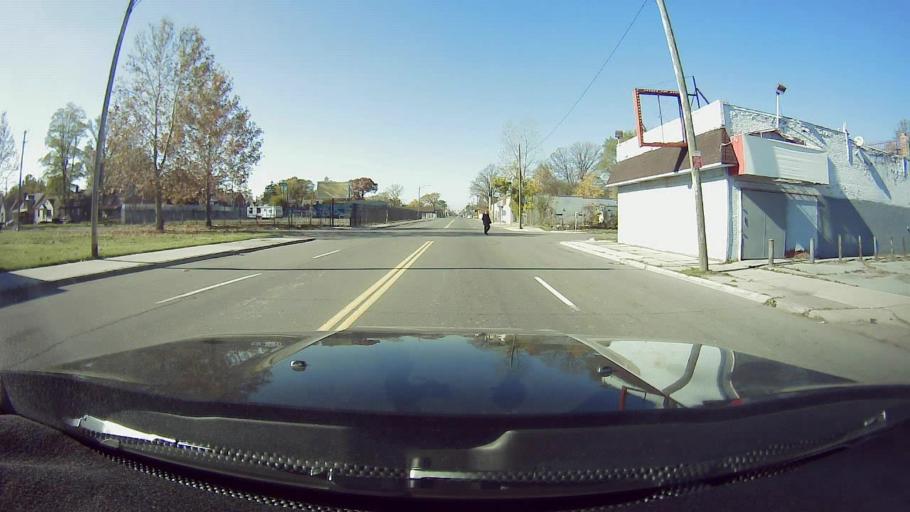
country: US
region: Michigan
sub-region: Wayne County
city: Dearborn
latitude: 42.3732
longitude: -83.1727
